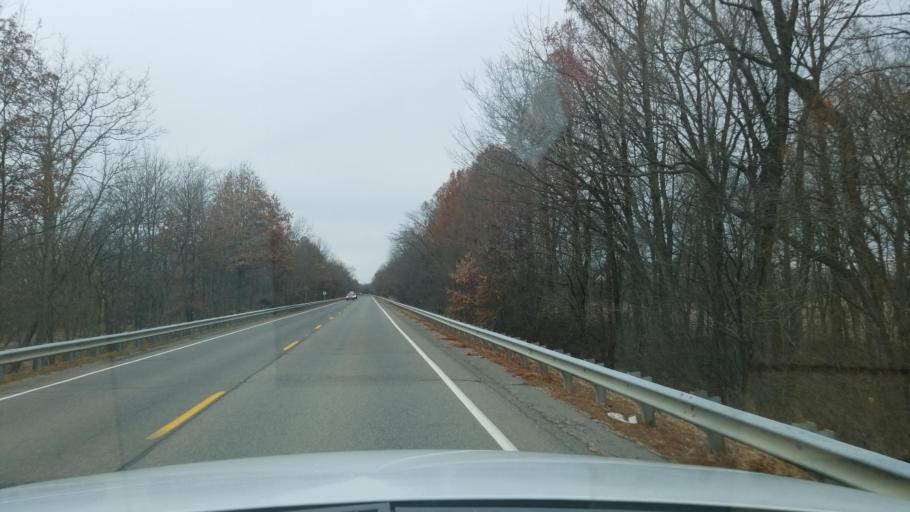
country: US
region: Indiana
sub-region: Posey County
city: Mount Vernon
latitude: 37.9355
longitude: -88.0082
